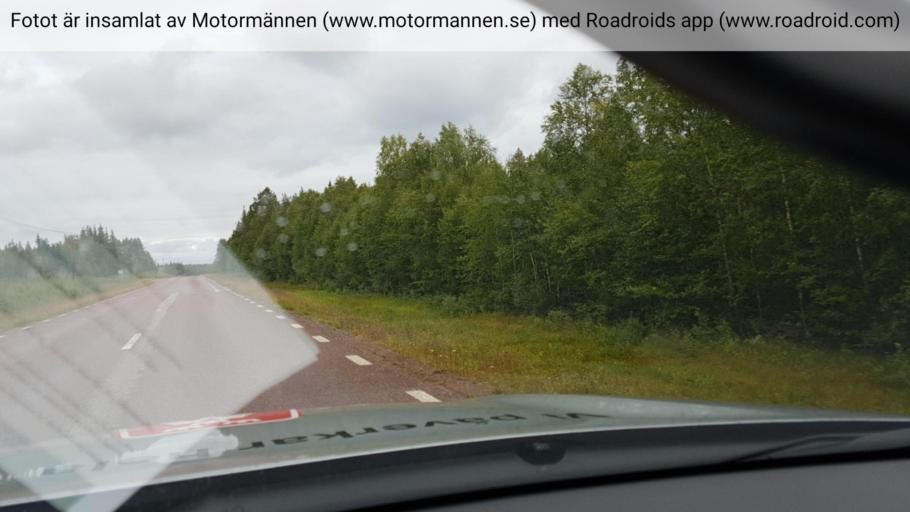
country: SE
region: Norrbotten
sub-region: Pajala Kommun
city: Pajala
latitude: 67.1226
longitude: 22.6058
